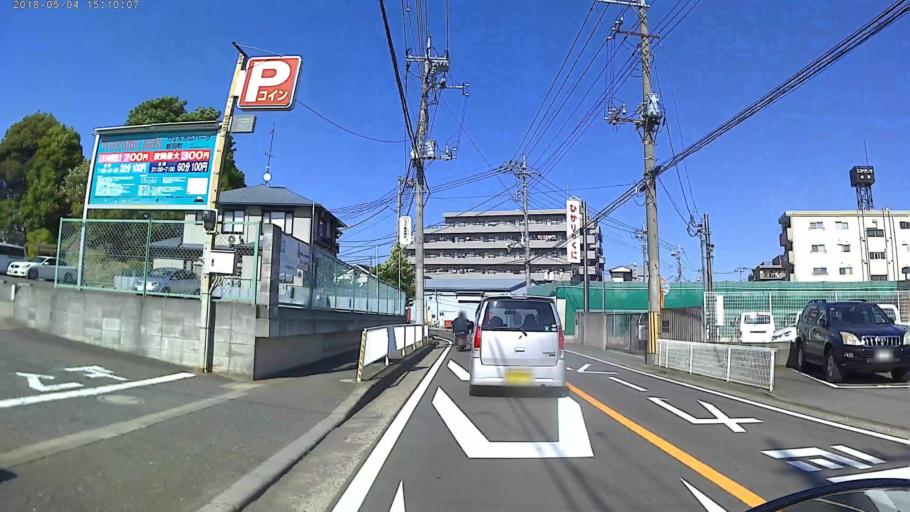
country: JP
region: Kanagawa
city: Yokohama
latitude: 35.5209
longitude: 139.6102
